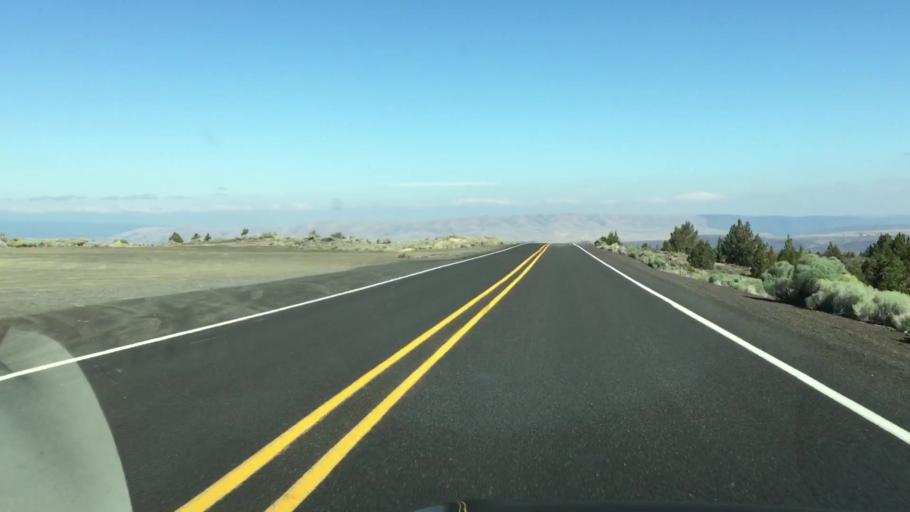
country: US
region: Oregon
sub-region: Jefferson County
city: Warm Springs
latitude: 45.0858
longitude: -121.0267
